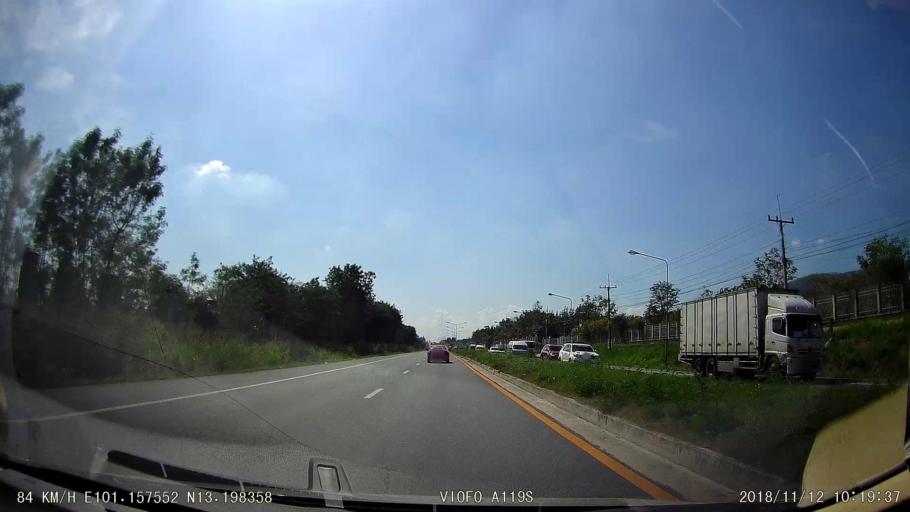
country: TH
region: Chon Buri
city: Ban Bueng
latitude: 13.1979
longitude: 101.1576
